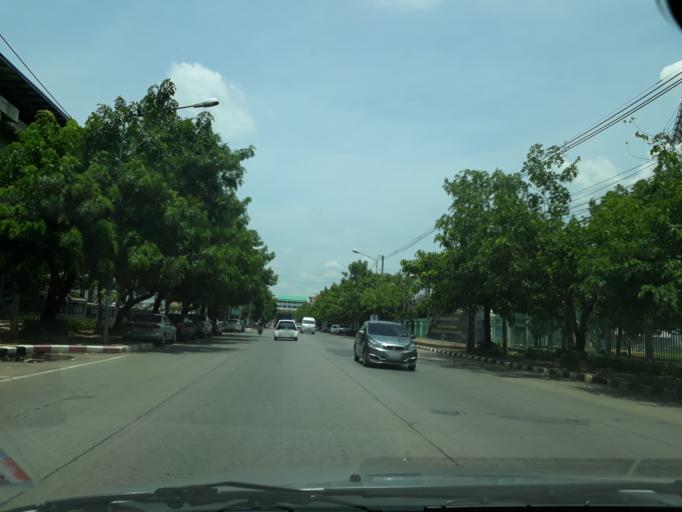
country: TH
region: Khon Kaen
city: Khon Kaen
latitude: 16.4142
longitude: 102.8277
